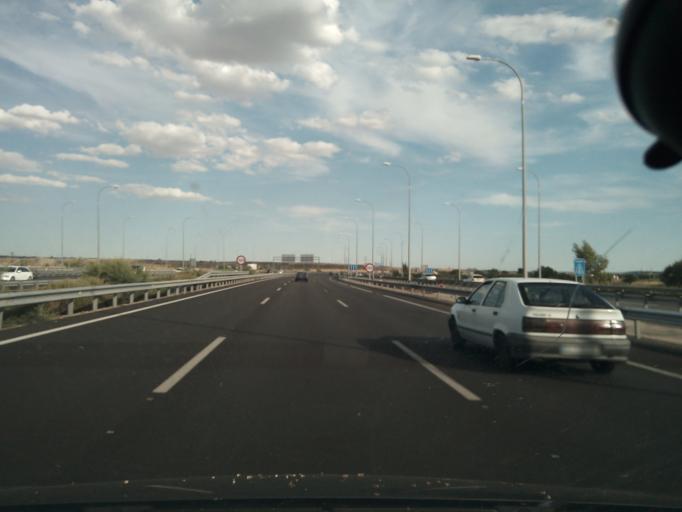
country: ES
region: Madrid
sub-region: Provincia de Madrid
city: San Fernando de Henares
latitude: 40.4321
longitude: -3.5033
